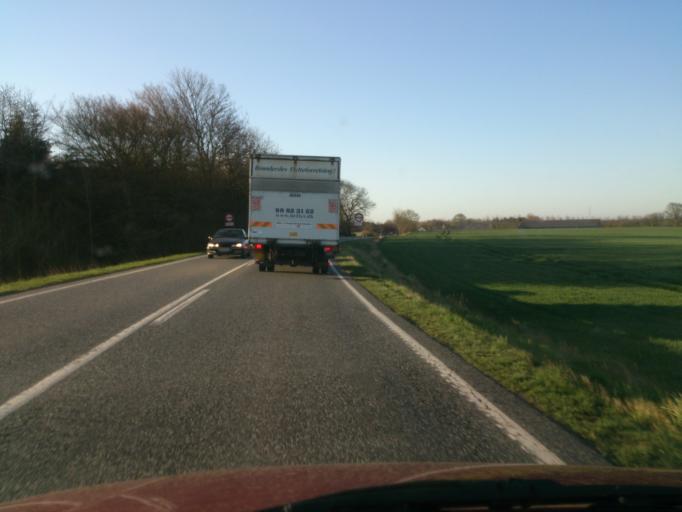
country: DK
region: Central Jutland
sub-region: Viborg Kommune
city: Bjerringbro
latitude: 56.4160
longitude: 9.6745
